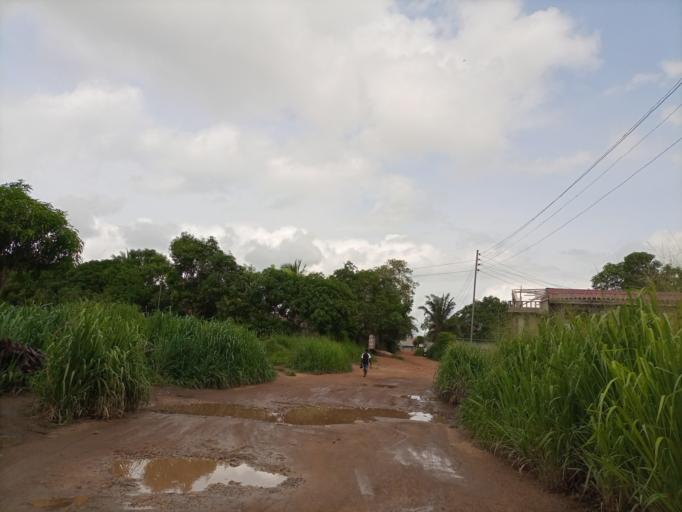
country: SL
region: Southern Province
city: Bo
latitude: 7.9702
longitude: -11.7624
